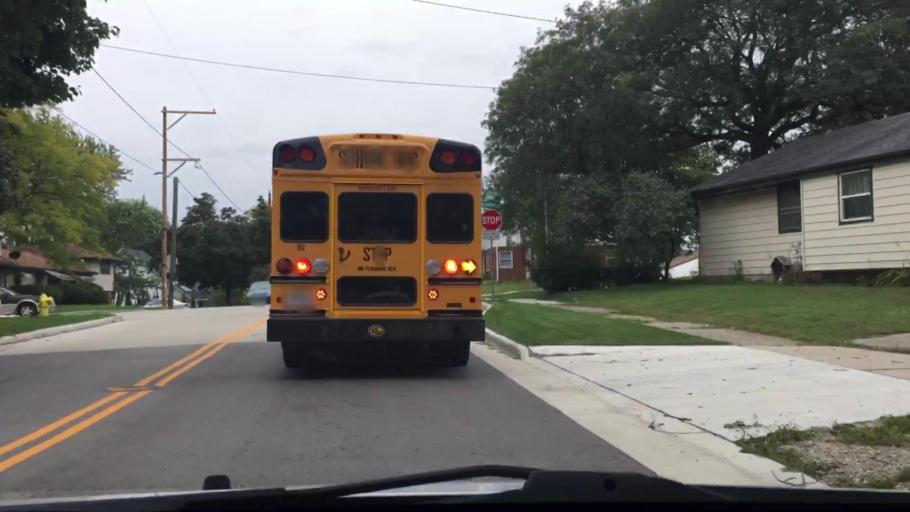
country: US
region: Wisconsin
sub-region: Waukesha County
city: Waukesha
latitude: 43.0139
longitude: -88.2128
